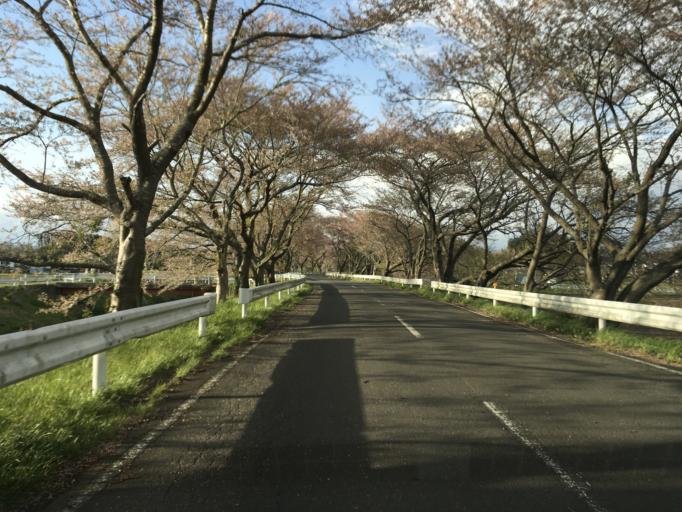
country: JP
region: Miyagi
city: Wakuya
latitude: 38.6543
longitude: 141.1463
